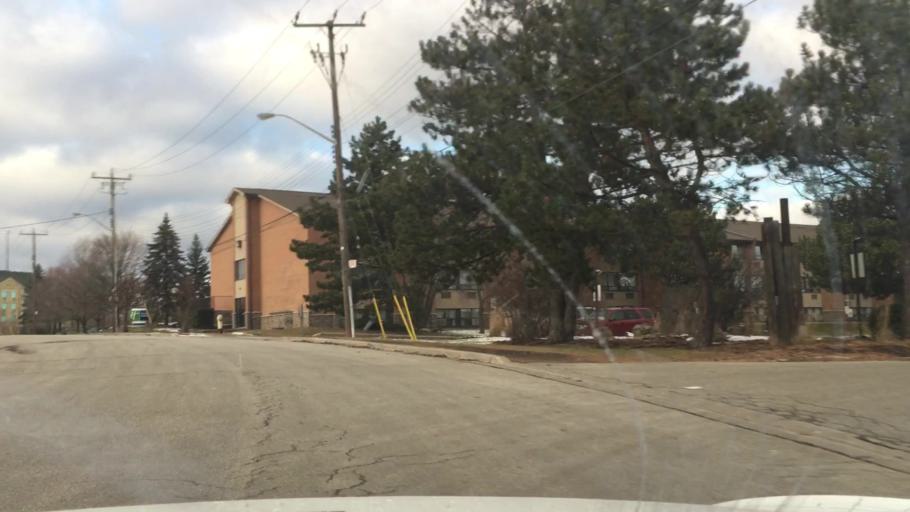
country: CA
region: Ontario
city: Scarborough
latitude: 43.7822
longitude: -79.2353
